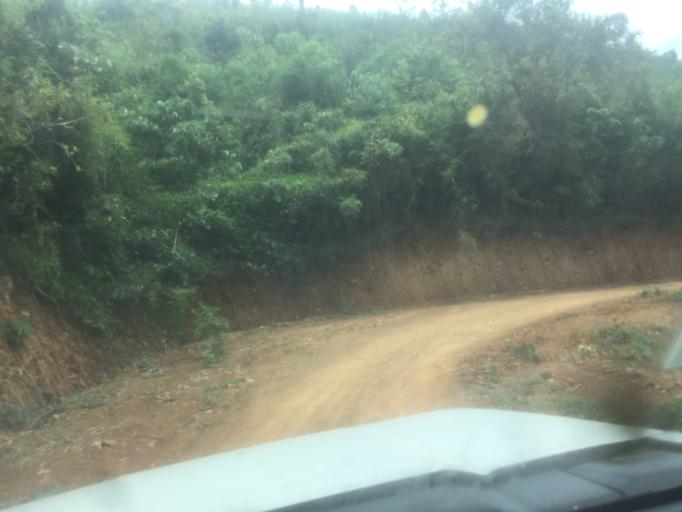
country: LA
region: Phongsali
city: Khoa
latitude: 20.9272
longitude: 102.5361
